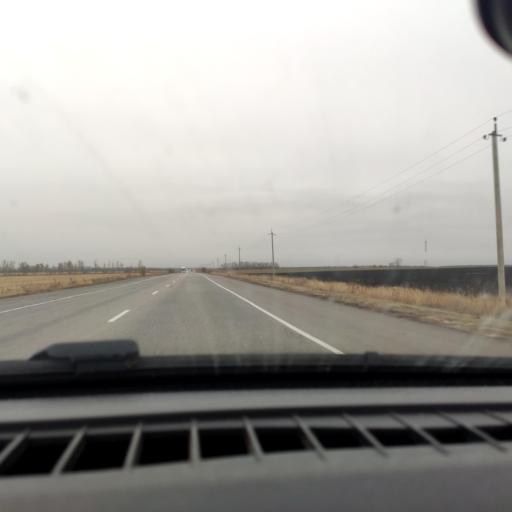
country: RU
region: Voronezj
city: Strelitsa
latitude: 51.5556
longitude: 38.9726
